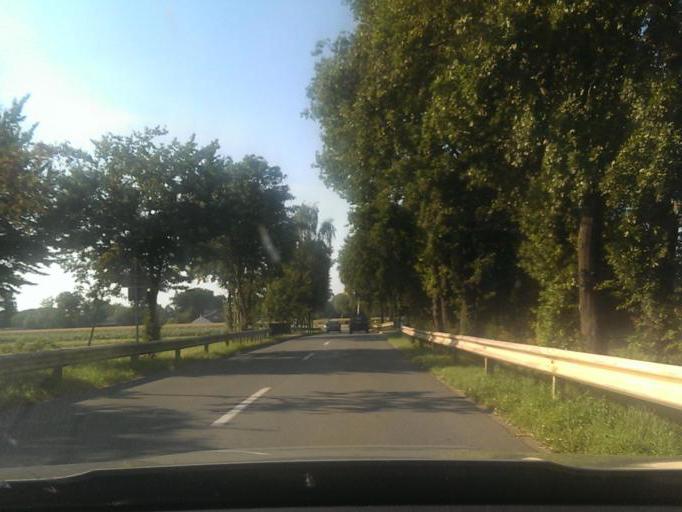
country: DE
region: North Rhine-Westphalia
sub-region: Regierungsbezirk Detmold
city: Delbruck
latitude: 51.7407
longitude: 8.5944
